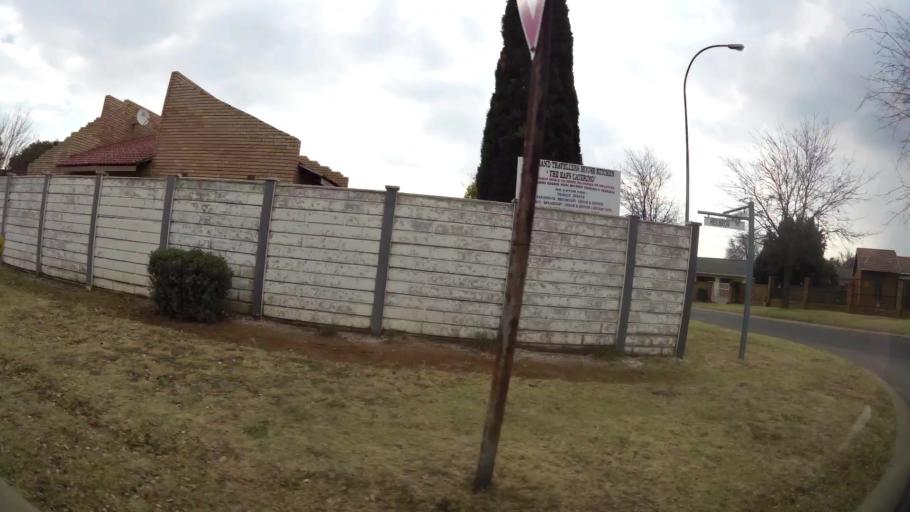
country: ZA
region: Gauteng
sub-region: Ekurhuleni Metropolitan Municipality
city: Benoni
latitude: -26.1229
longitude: 28.3631
